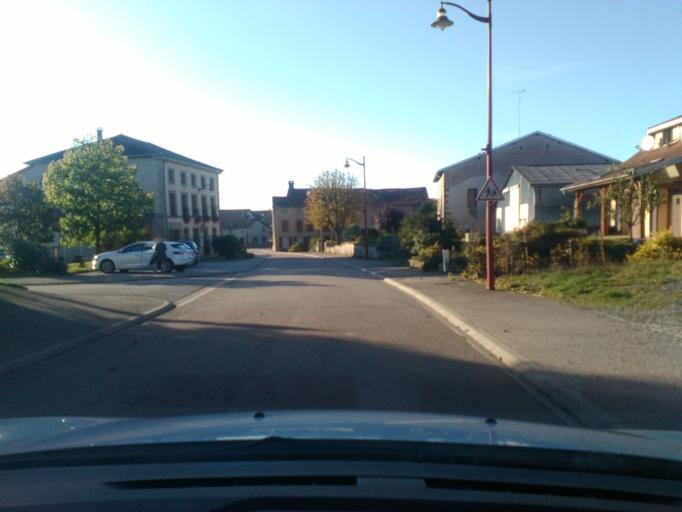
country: FR
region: Lorraine
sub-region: Departement des Vosges
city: Rambervillers
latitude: 48.2950
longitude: 6.6064
